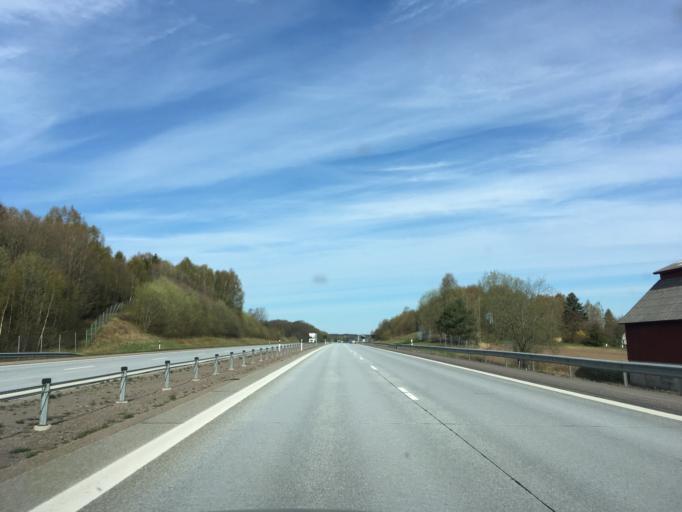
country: SE
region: Halland
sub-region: Halmstads Kommun
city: Getinge
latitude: 56.8702
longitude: 12.6414
